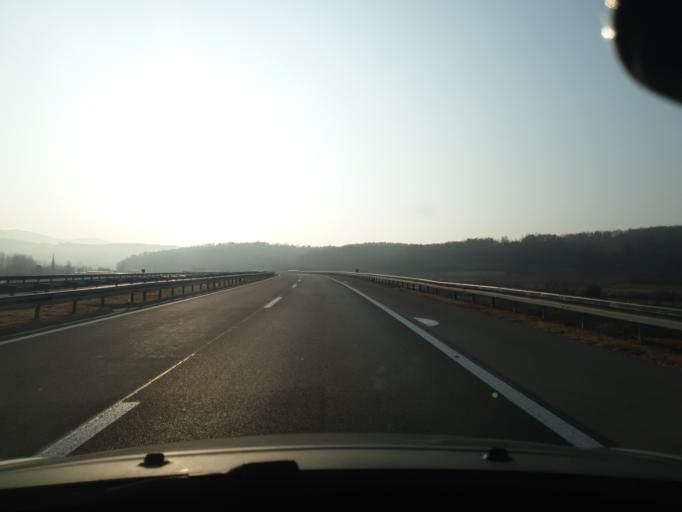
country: RS
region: Central Serbia
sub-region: Jablanicki Okrug
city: Vlasotince
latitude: 42.9170
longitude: 22.0340
